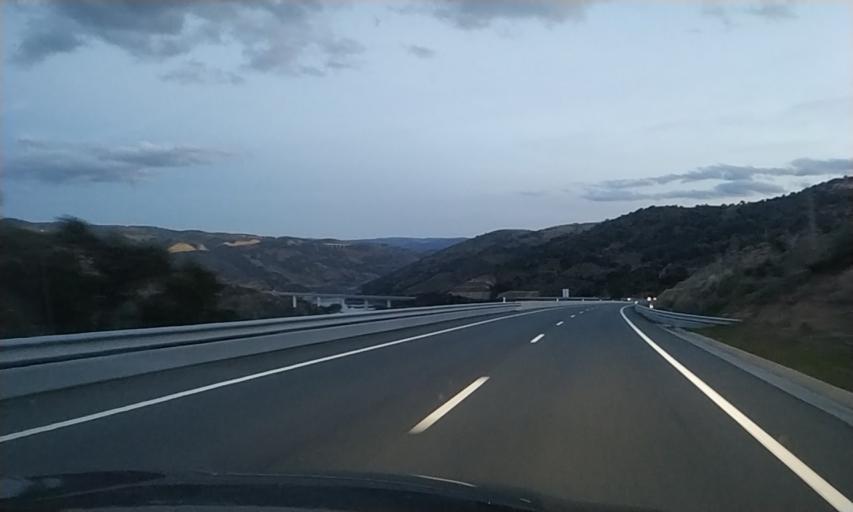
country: PT
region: Braganca
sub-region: Alfandega da Fe
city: Alfandega da Fe
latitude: 41.3170
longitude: -6.9287
